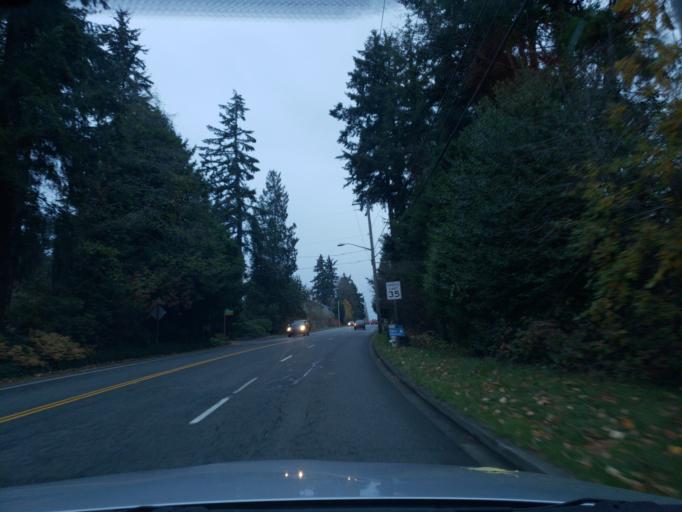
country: US
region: Washington
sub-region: King County
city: Inglewood-Finn Hill
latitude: 47.7342
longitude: -122.2186
